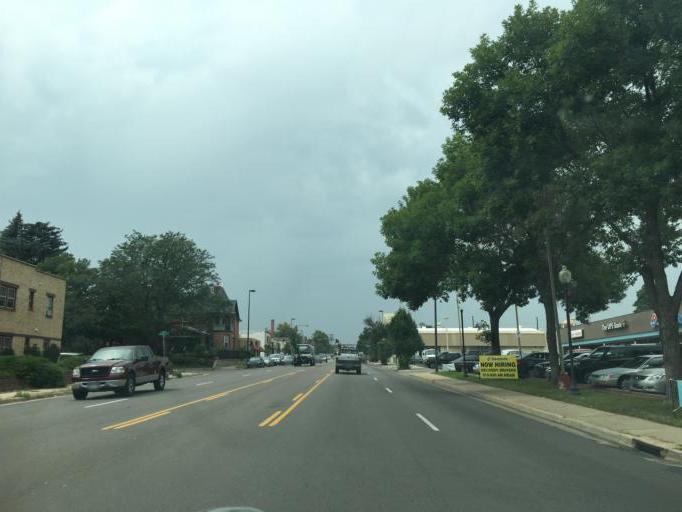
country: US
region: Colorado
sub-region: Adams County
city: Berkley
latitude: 39.7693
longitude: -105.0227
